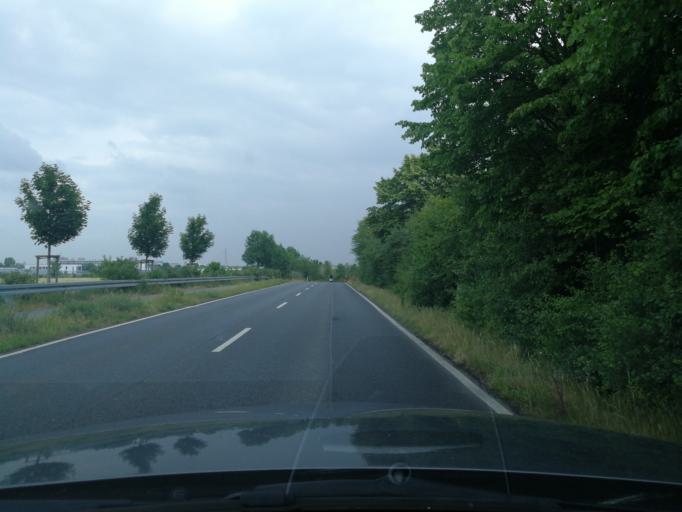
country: DE
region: North Rhine-Westphalia
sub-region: Regierungsbezirk Dusseldorf
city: Dusseldorf
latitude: 51.1619
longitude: 6.7491
